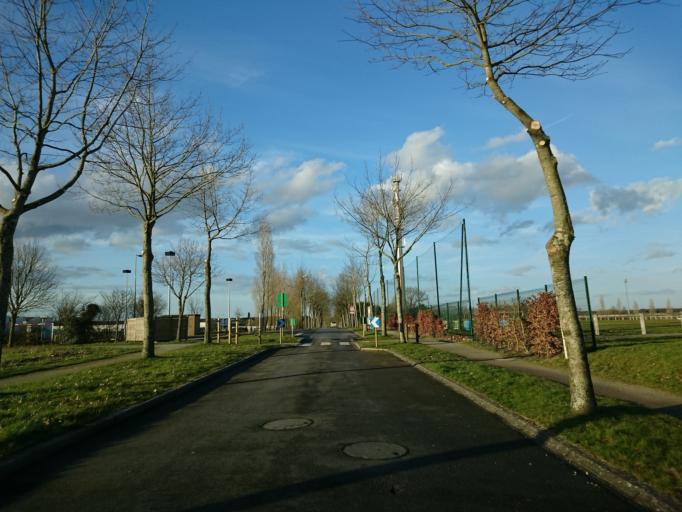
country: FR
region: Brittany
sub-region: Departement d'Ille-et-Vilaine
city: Crevin
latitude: 47.9397
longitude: -1.6619
